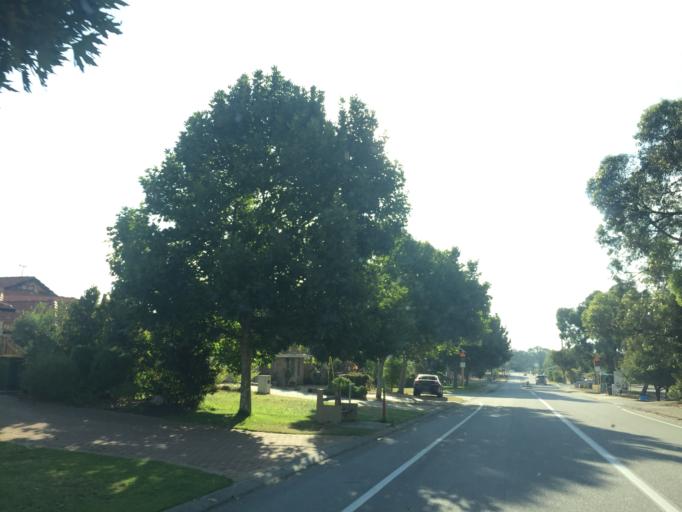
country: AU
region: Western Australia
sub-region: City of Cockburn
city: City of Cockburn
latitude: -32.0928
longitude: 115.8417
